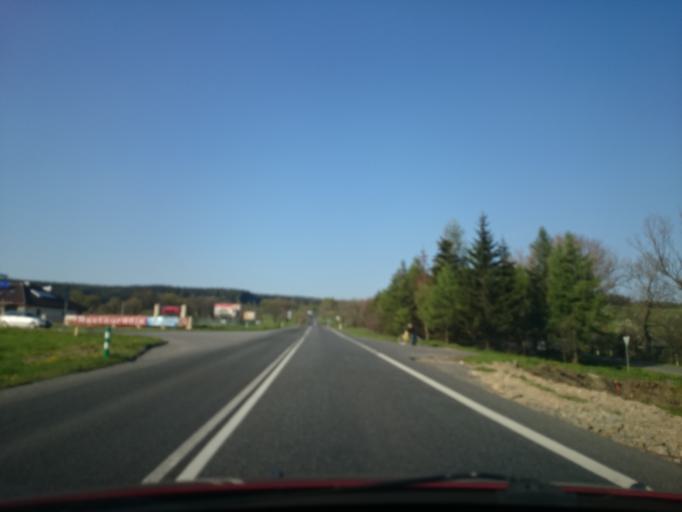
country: PL
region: Lower Silesian Voivodeship
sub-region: Powiat klodzki
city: Szczytna
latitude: 50.4166
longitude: 16.4506
